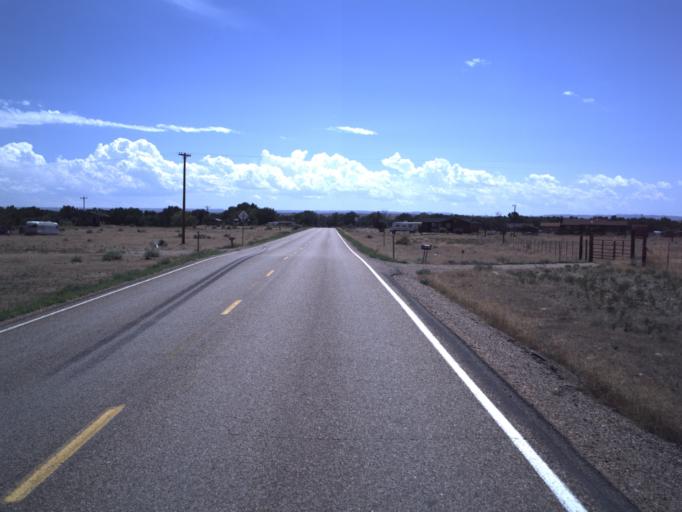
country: US
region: Utah
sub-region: Duchesne County
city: Roosevelt
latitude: 40.0943
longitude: -109.6795
